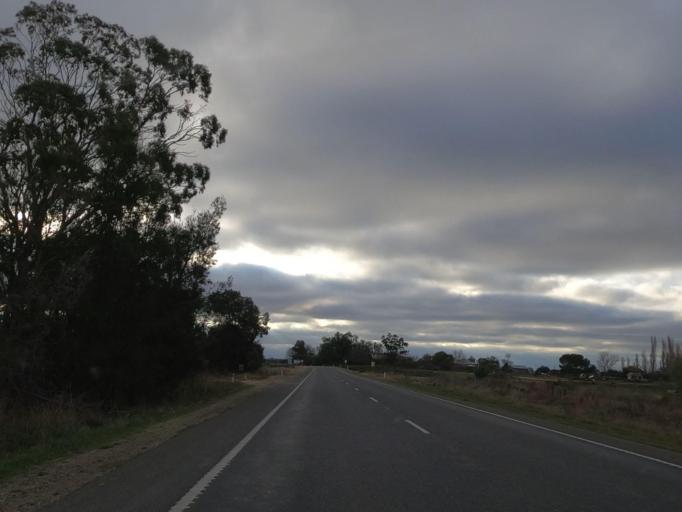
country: AU
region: Victoria
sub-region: Swan Hill
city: Swan Hill
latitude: -35.7261
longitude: 143.8907
